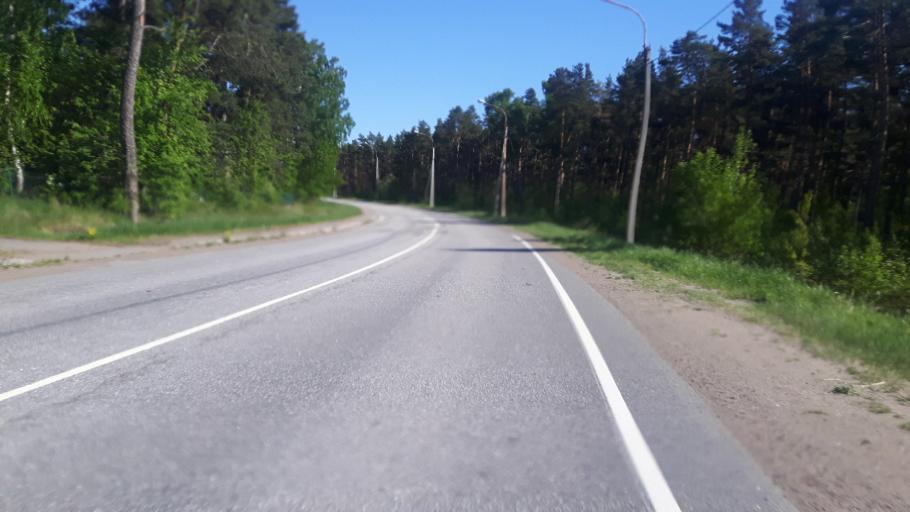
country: RU
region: Leningrad
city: Sosnovyy Bor
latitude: 60.1932
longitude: 29.0078
